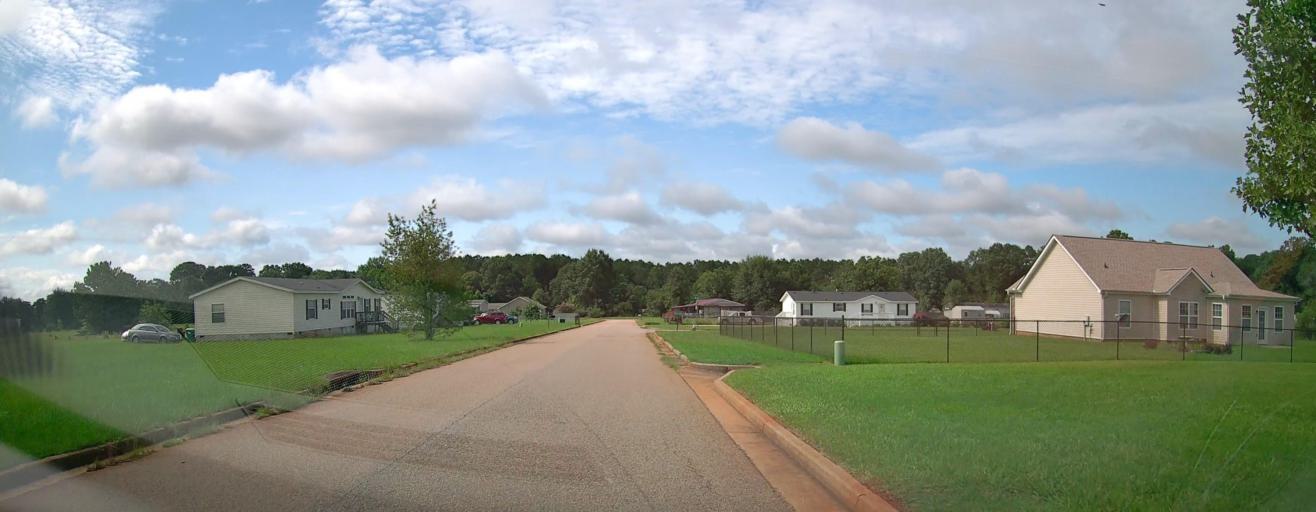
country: US
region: Georgia
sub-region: Houston County
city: Centerville
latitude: 32.6466
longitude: -83.7205
